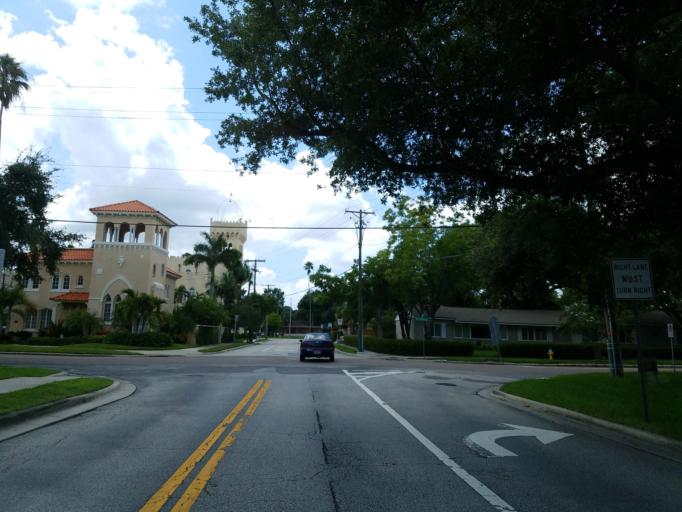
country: US
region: Florida
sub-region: Hillsborough County
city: Tampa
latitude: 27.9352
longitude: -82.4572
